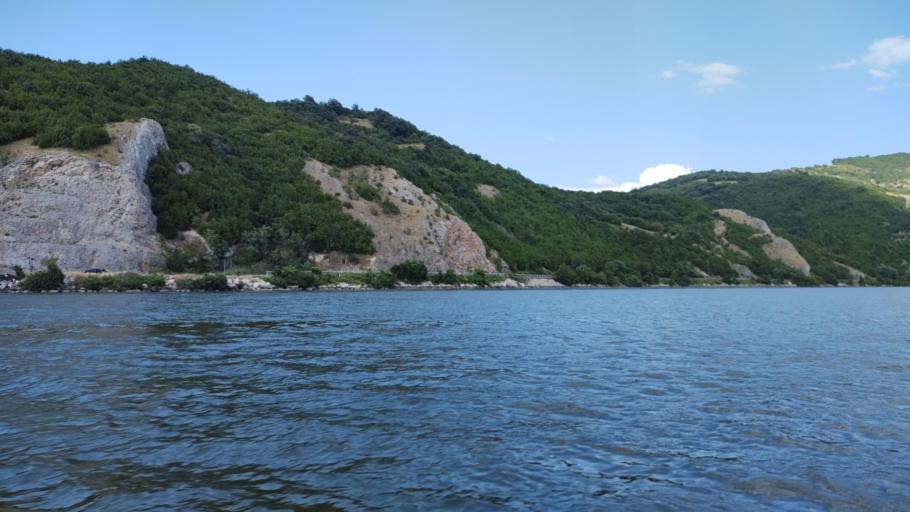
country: RO
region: Caras-Severin
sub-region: Comuna Pescari
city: Coronini
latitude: 44.6689
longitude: 21.6828
